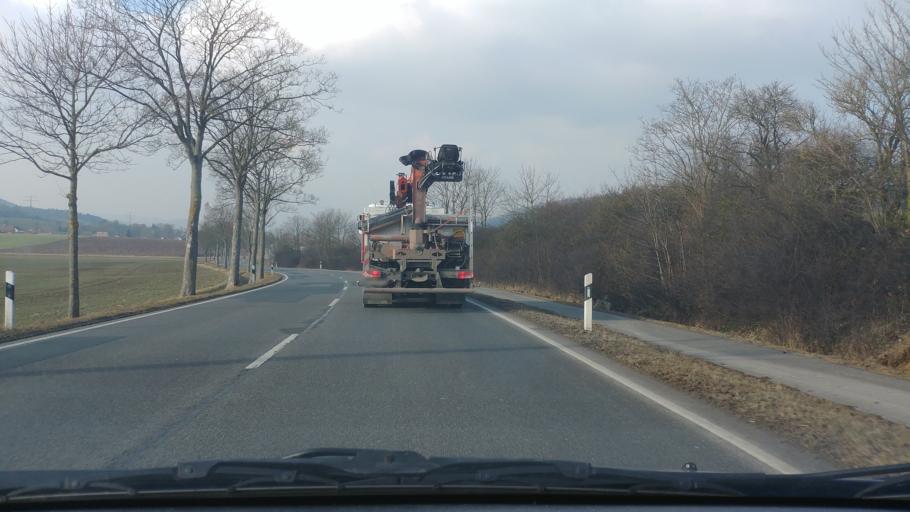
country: DE
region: Lower Saxony
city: Freden
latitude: 51.9012
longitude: 9.8669
